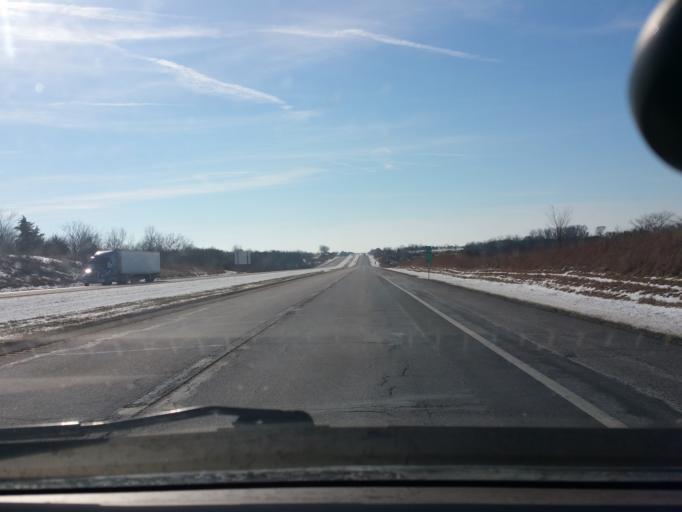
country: US
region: Iowa
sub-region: Decatur County
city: Lamoni
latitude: 40.4517
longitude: -93.9813
